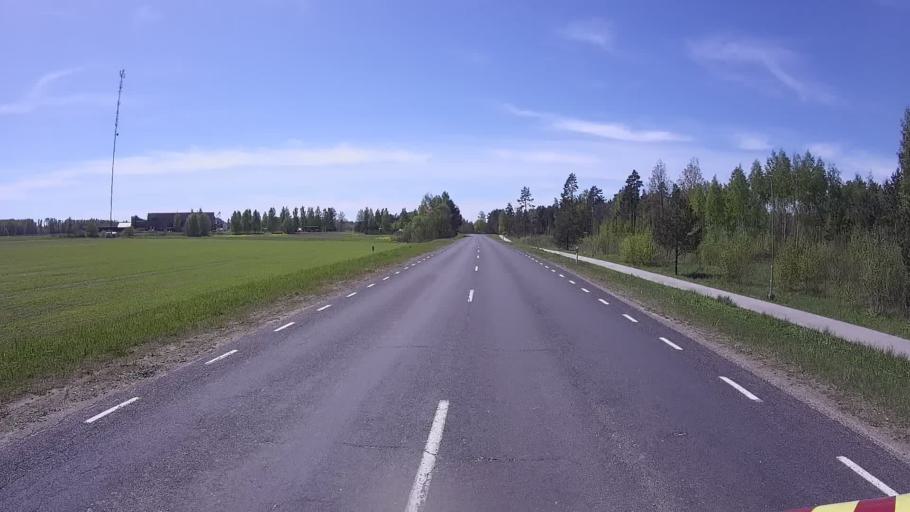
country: EE
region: Polvamaa
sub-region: Raepina vald
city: Rapina
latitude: 57.9984
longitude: 27.3387
